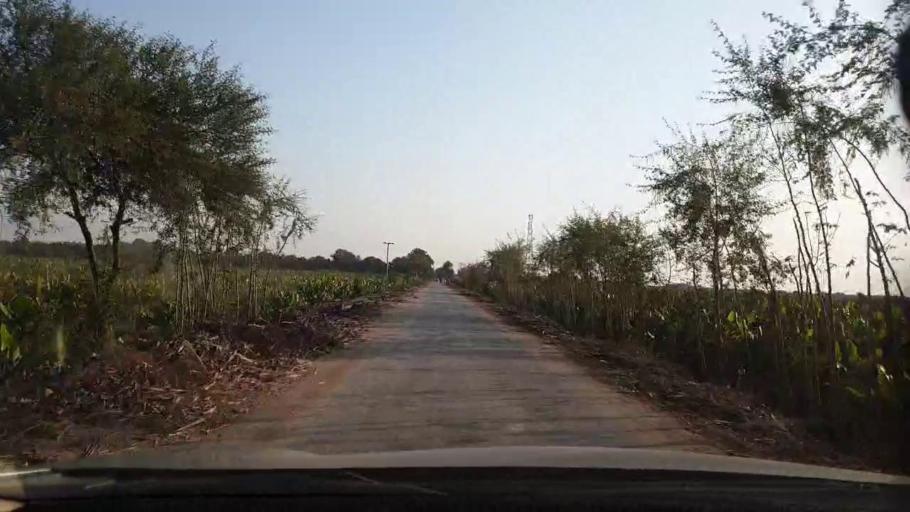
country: PK
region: Sindh
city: Berani
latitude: 25.6427
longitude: 68.8084
